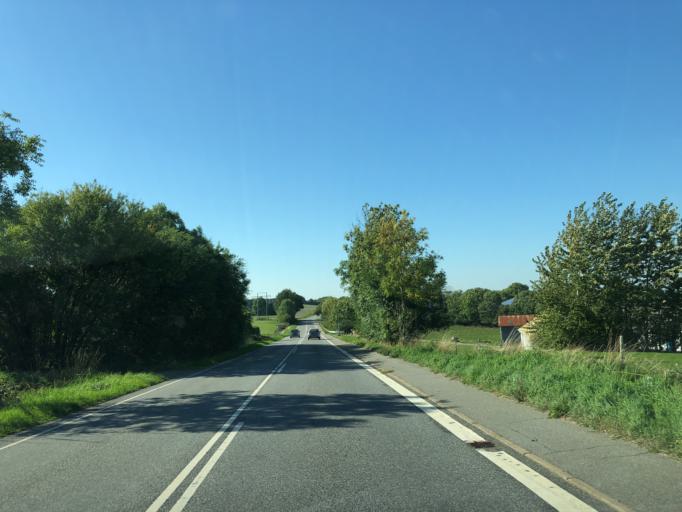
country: DK
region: South Denmark
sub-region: Aabenraa Kommune
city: Lojt Kirkeby
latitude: 55.0150
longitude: 9.4813
